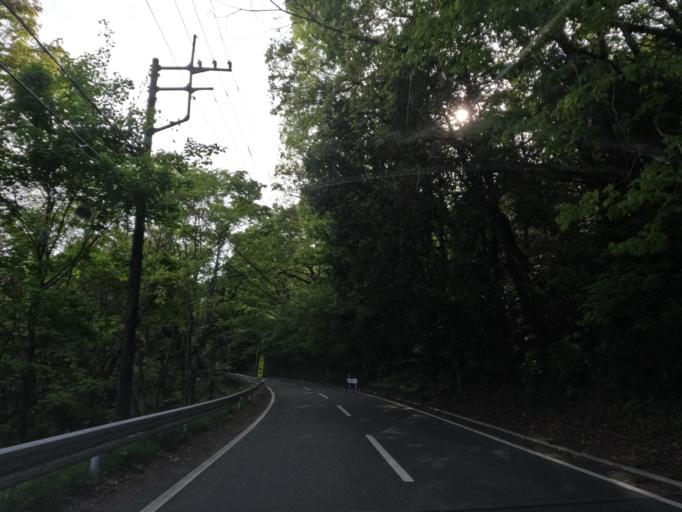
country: JP
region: Saitama
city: Chichibu
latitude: 36.0824
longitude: 139.0983
